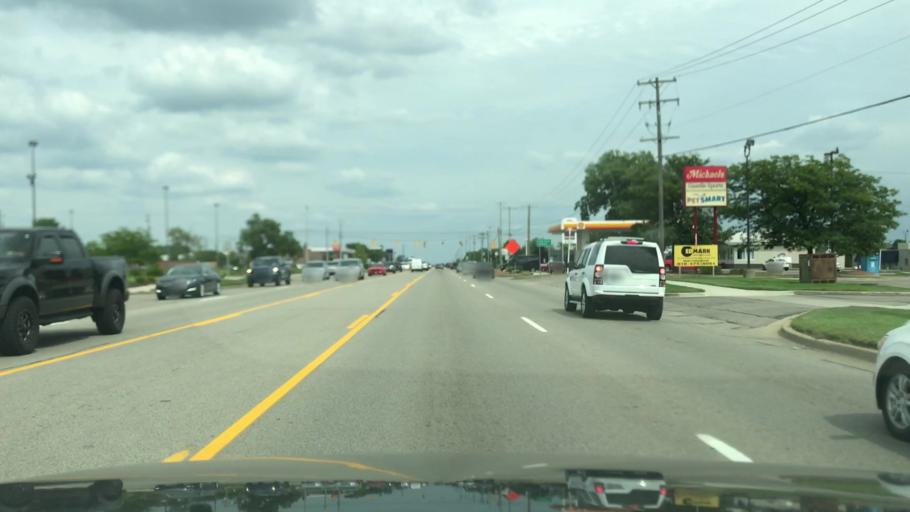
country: US
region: Michigan
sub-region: Kent County
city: East Grand Rapids
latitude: 42.9125
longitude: -85.5709
